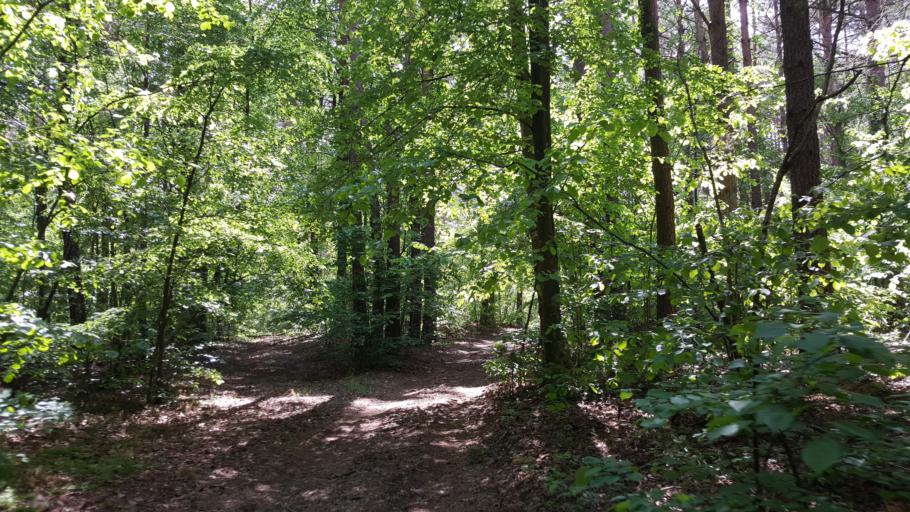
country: BY
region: Brest
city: Kamyanyets
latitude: 52.4504
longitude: 24.0117
